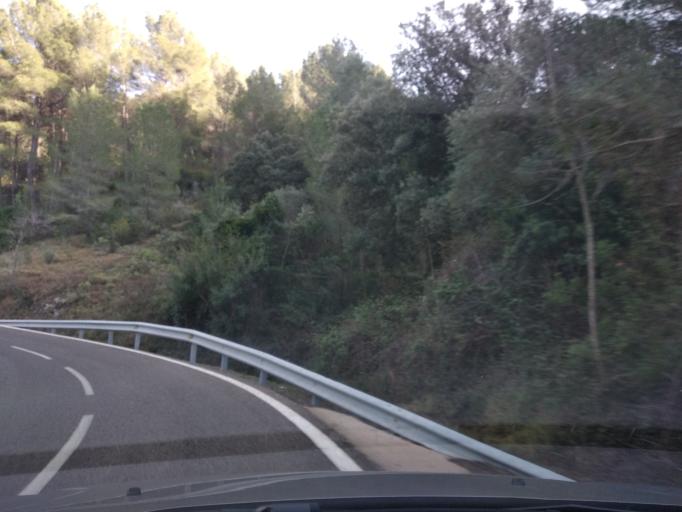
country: ES
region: Catalonia
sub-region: Provincia de Tarragona
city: la Morera de Montsant
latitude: 41.2429
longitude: 0.7944
